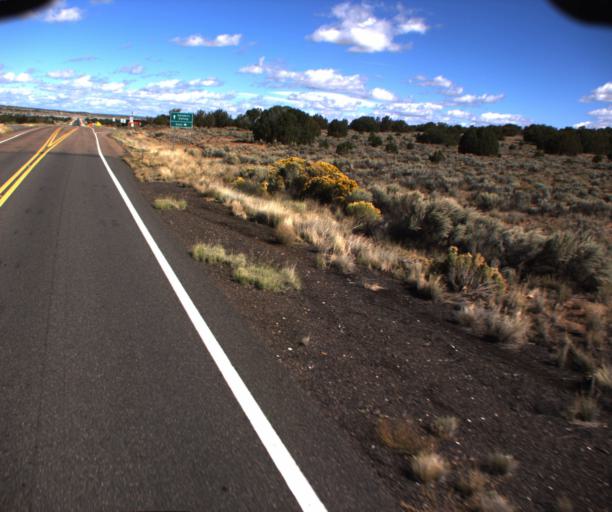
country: US
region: Arizona
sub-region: Apache County
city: Houck
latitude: 34.8999
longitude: -109.2381
